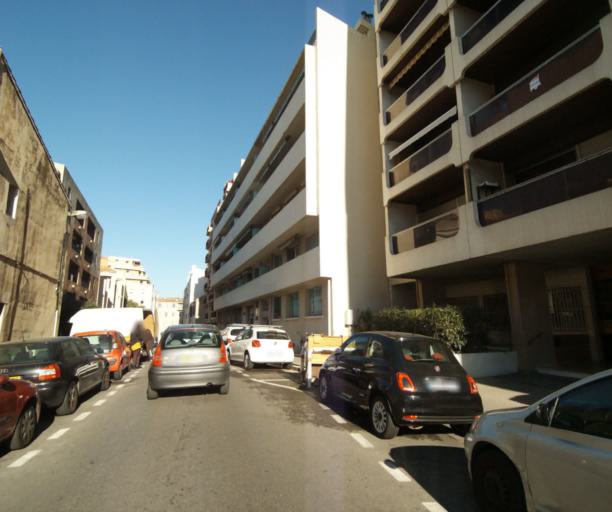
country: FR
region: Provence-Alpes-Cote d'Azur
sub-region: Departement des Bouches-du-Rhone
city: Marseille 05
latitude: 43.2865
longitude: 5.3948
